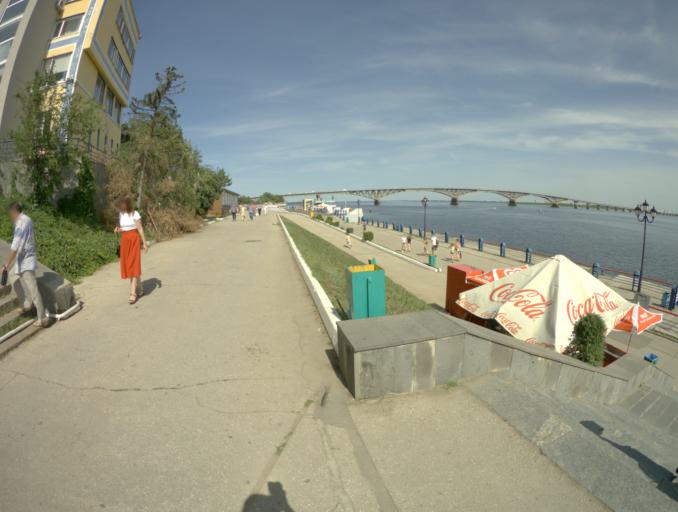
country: RU
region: Saratov
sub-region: Saratovskiy Rayon
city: Saratov
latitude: 51.5260
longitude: 46.0558
